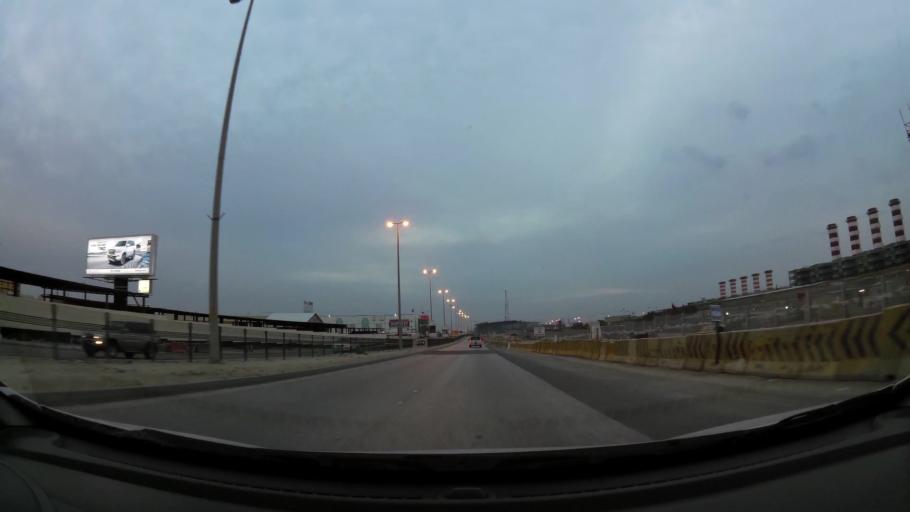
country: BH
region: Northern
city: Ar Rifa'
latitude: 26.1206
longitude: 50.5869
